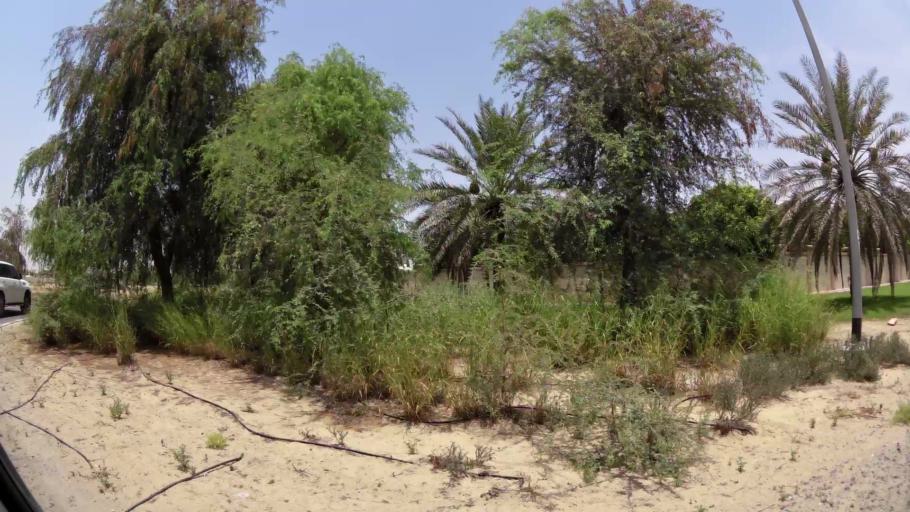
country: AE
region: Ash Shariqah
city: Sharjah
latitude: 25.2355
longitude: 55.4606
